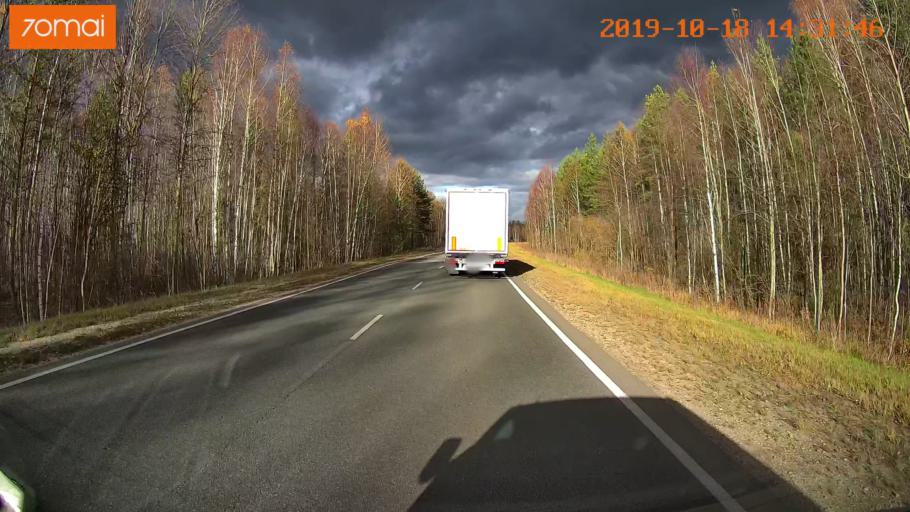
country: RU
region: Rjazan
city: Tuma
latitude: 55.1858
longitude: 40.5722
